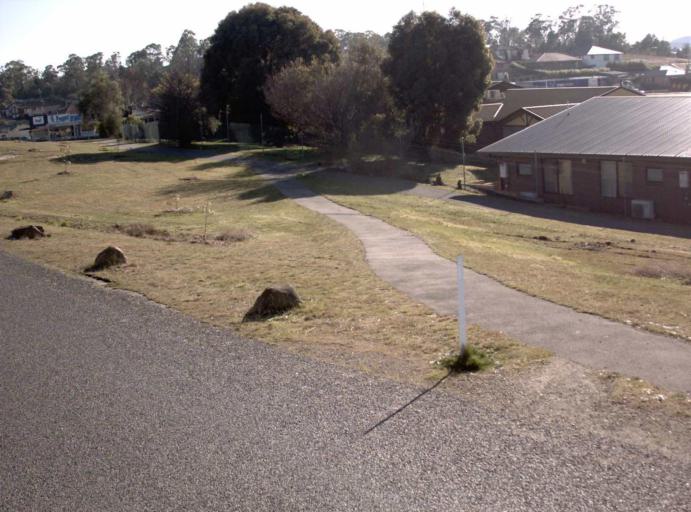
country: AU
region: Tasmania
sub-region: Launceston
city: Summerhill
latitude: -41.4720
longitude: 147.1345
